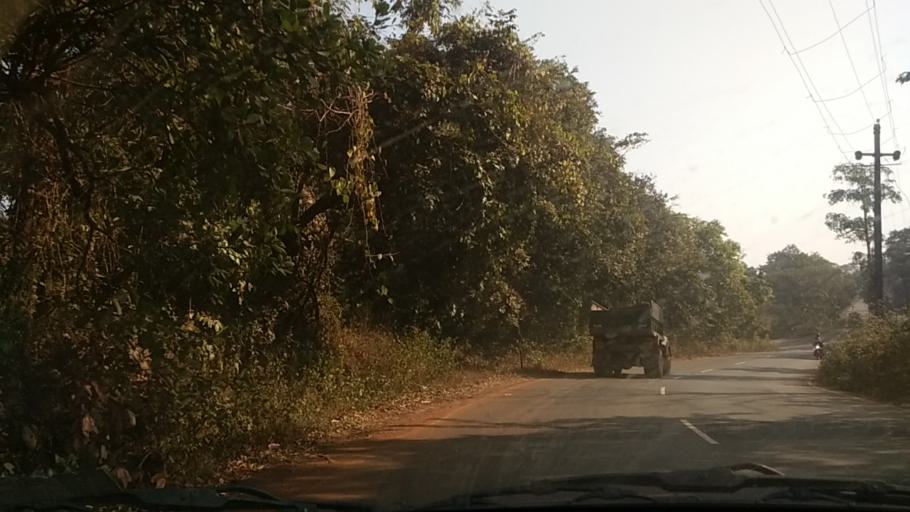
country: IN
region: Goa
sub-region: South Goa
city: Sanvordem
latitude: 15.2870
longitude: 74.1308
